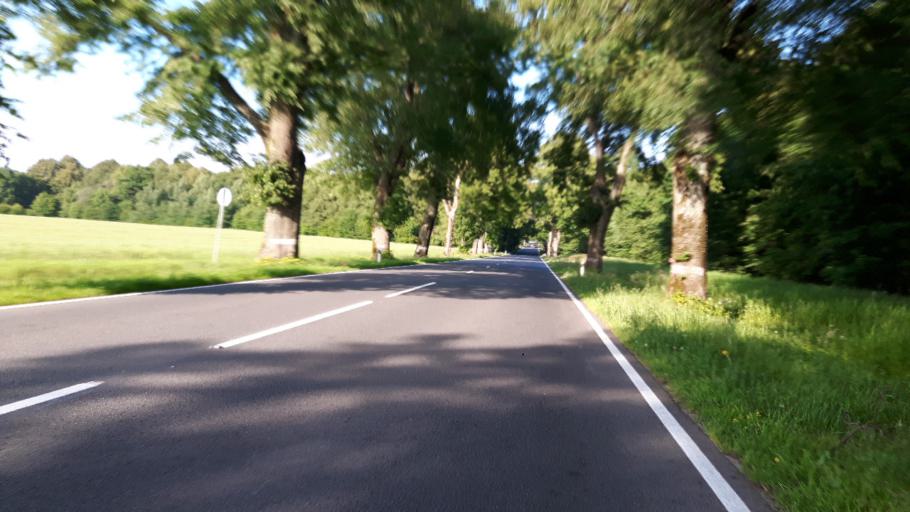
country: RU
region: Kaliningrad
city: Ladushkin
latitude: 54.4971
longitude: 20.0772
